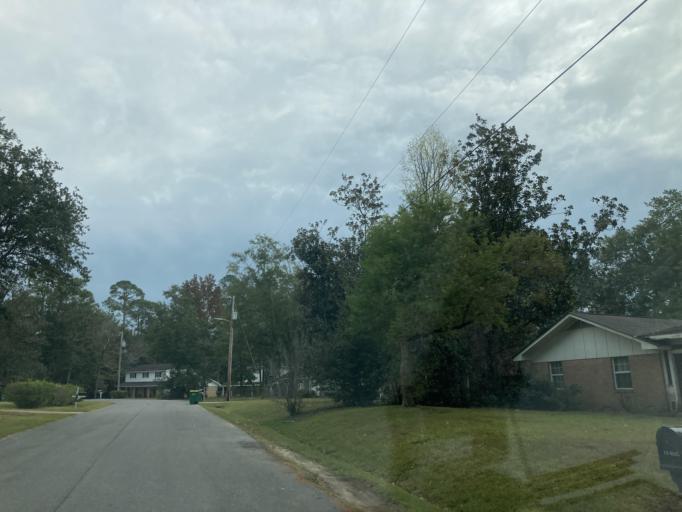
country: US
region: Mississippi
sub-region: Jackson County
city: Gulf Hills
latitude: 30.4317
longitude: -88.8429
